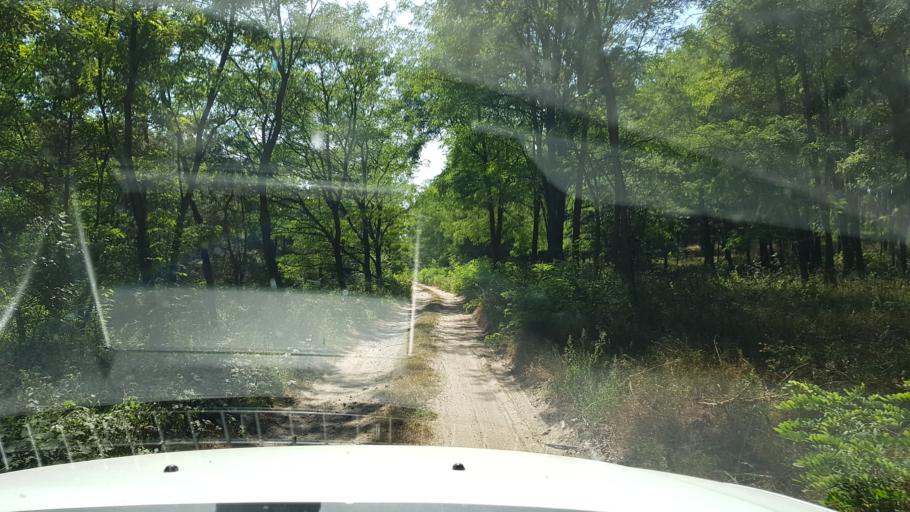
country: PL
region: West Pomeranian Voivodeship
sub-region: Powiat gryfinski
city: Cedynia
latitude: 52.8371
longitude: 14.2532
